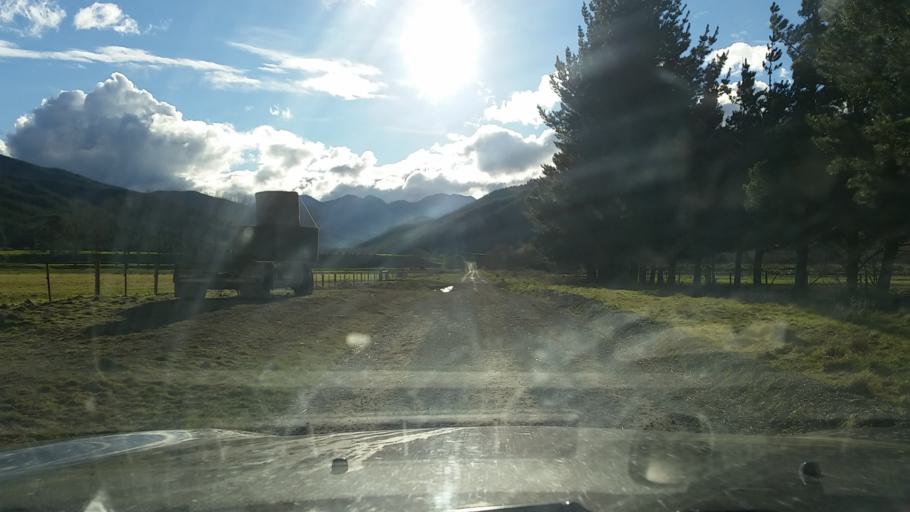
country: NZ
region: Nelson
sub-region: Nelson City
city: Nelson
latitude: -41.5689
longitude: 173.4525
